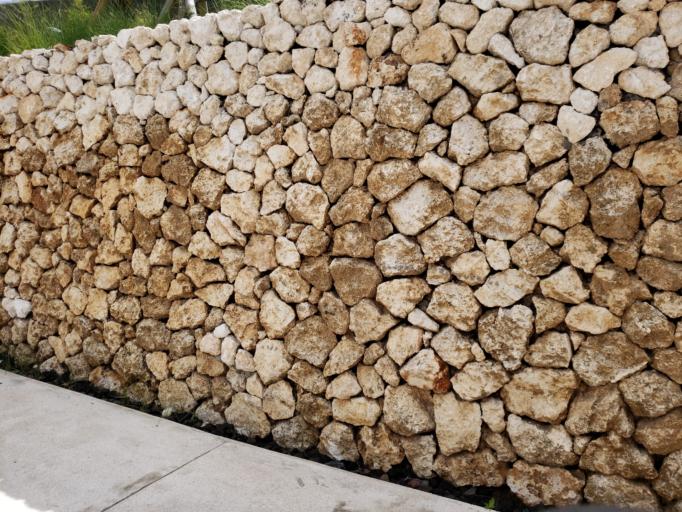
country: ID
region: Bali
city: Kangin
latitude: -8.8453
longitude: 115.1311
